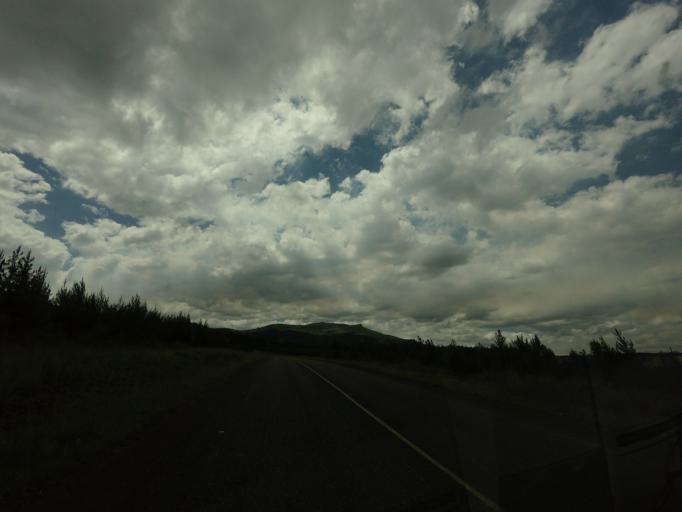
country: ZA
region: Mpumalanga
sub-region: Ehlanzeni District
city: Graksop
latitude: -24.9747
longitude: 30.8078
